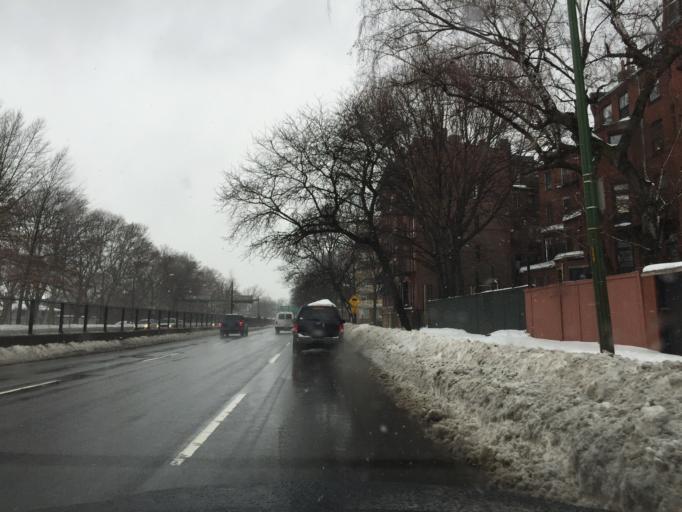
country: US
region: Massachusetts
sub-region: Suffolk County
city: Boston
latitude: 42.3580
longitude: -71.0725
